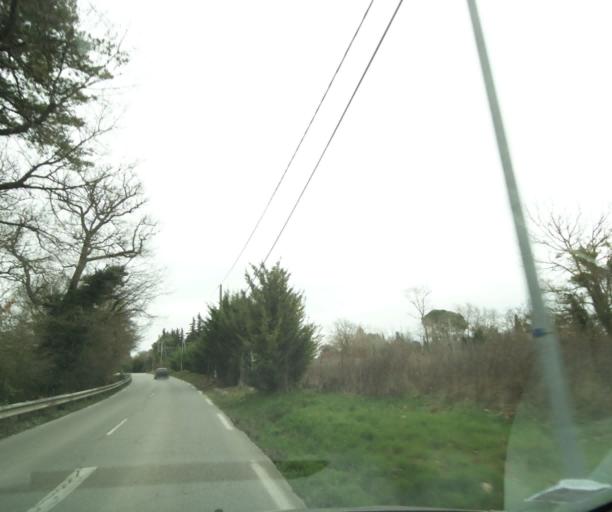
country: FR
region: Provence-Alpes-Cote d'Azur
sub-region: Departement des Bouches-du-Rhone
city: Venelles
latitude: 43.5786
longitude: 5.4412
